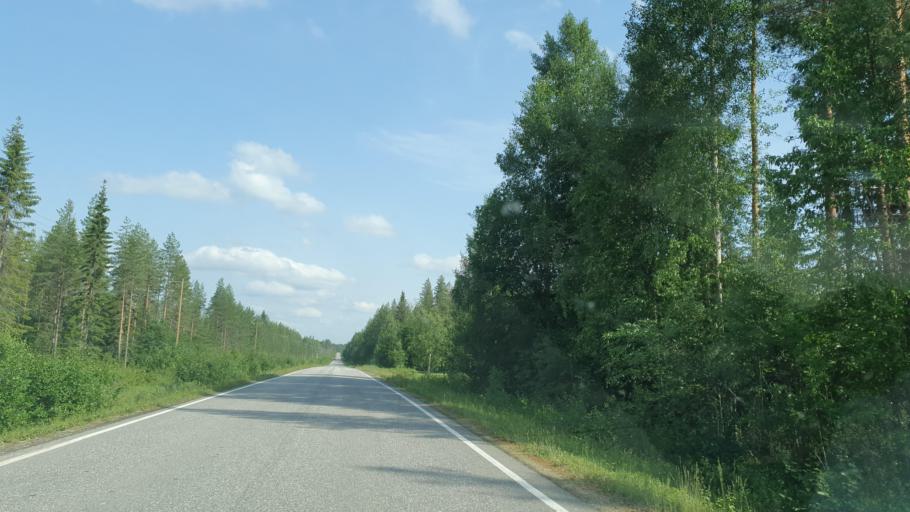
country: FI
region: Kainuu
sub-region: Kehys-Kainuu
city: Kuhmo
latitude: 64.0912
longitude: 29.8008
